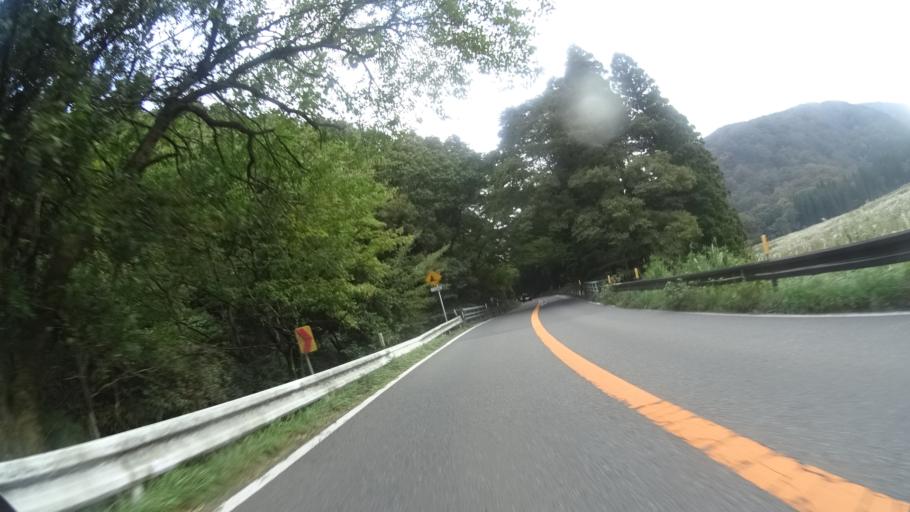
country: JP
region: Oita
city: Beppu
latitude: 33.2734
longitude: 131.4163
